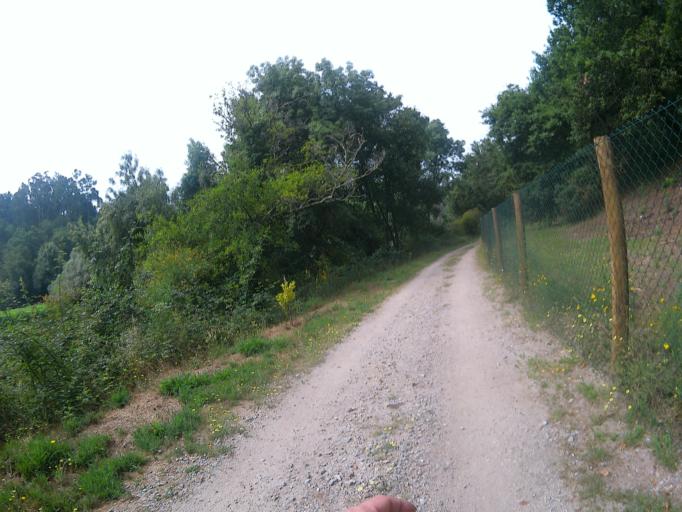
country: PT
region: Viana do Castelo
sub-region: Ponte de Lima
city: Ponte de Lima
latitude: 41.7847
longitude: -8.5226
